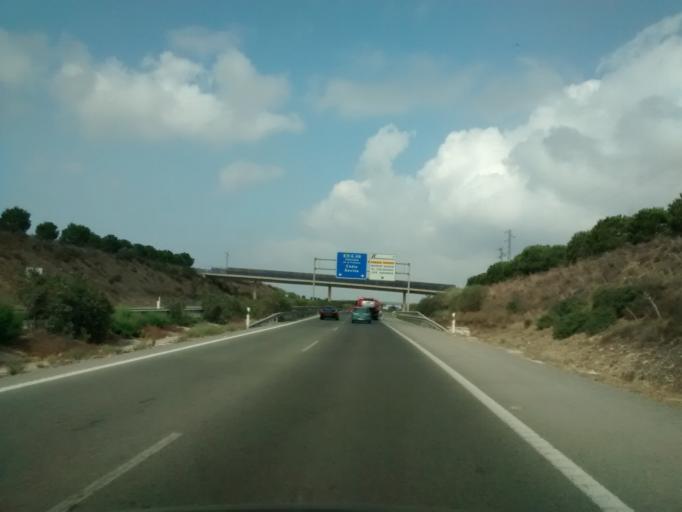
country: ES
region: Andalusia
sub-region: Provincia de Cadiz
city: Conil de la Frontera
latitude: 36.3440
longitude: -6.0527
